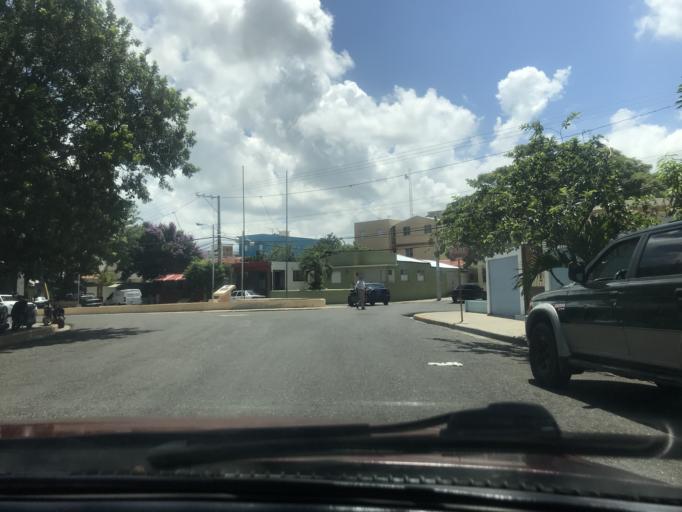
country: DO
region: Santiago
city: Santiago de los Caballeros
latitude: 19.4666
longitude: -70.7002
